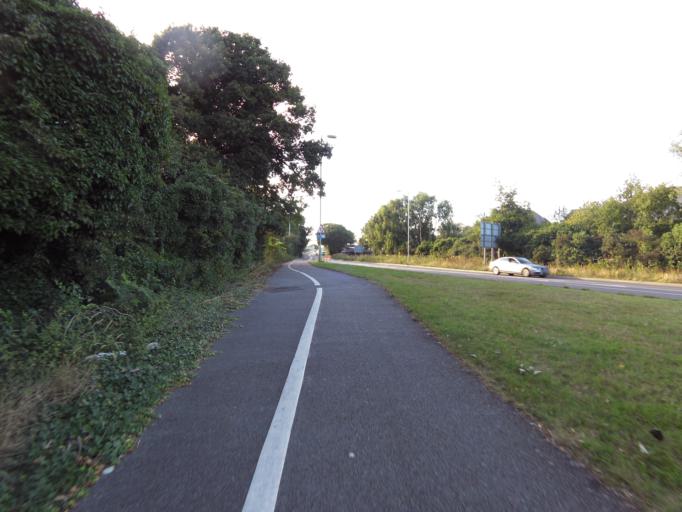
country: GB
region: England
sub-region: Suffolk
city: Kesgrave
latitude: 52.0263
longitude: 1.2064
